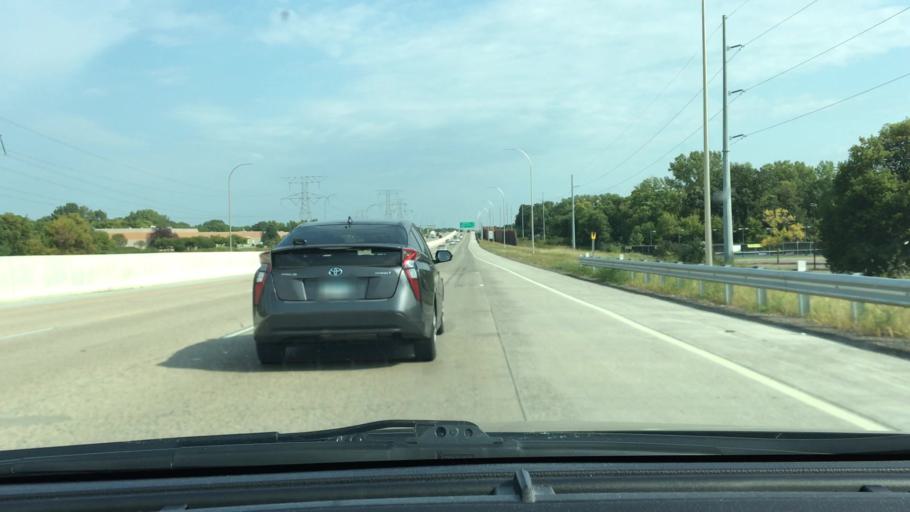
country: US
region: Minnesota
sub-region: Hennepin County
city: Plymouth
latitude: 45.0165
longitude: -93.4563
